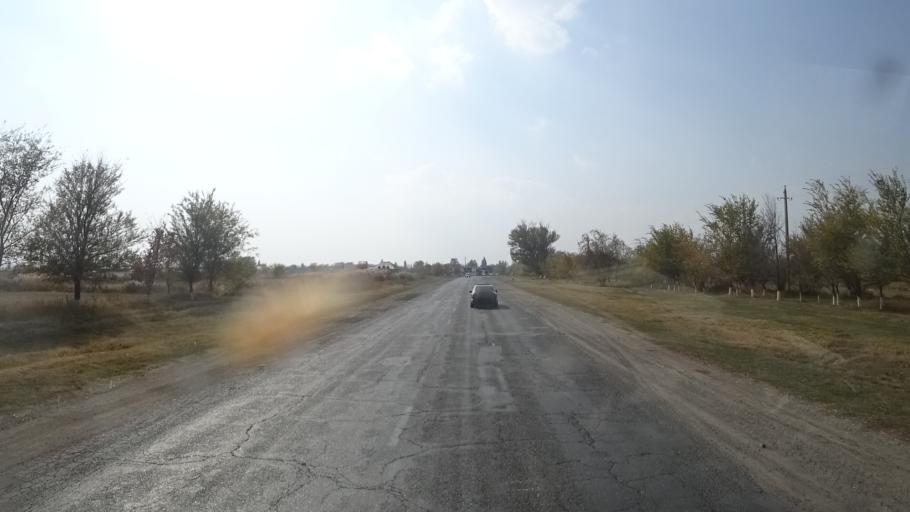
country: KZ
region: Zhambyl
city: Taraz
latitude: 42.9355
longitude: 71.4418
